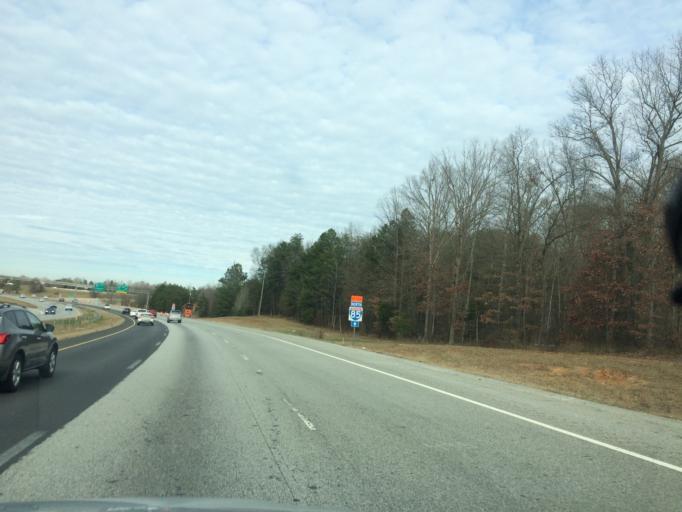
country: US
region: South Carolina
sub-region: Spartanburg County
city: Fairforest
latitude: 34.9721
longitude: -82.0067
